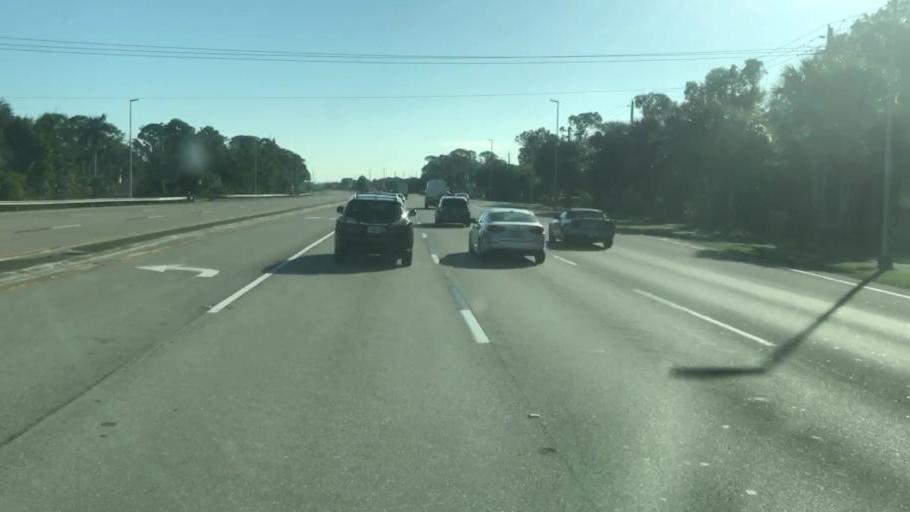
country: US
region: Florida
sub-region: Lee County
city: Villas
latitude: 26.5463
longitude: -81.8617
